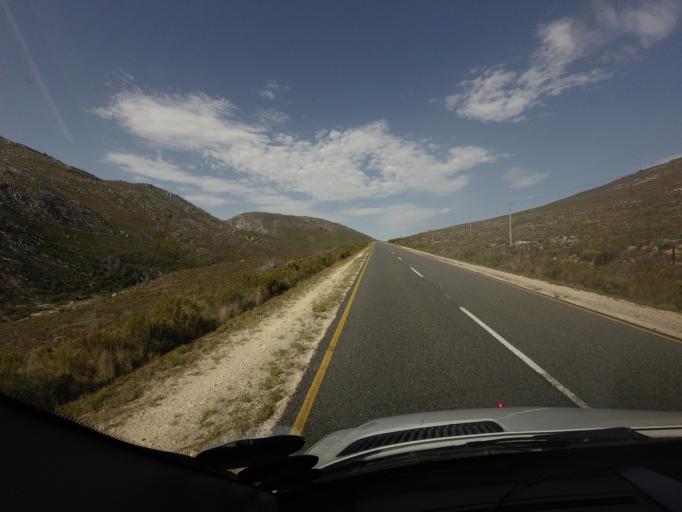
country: ZA
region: Western Cape
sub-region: Overberg District Municipality
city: Caledon
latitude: -34.4085
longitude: 19.5695
